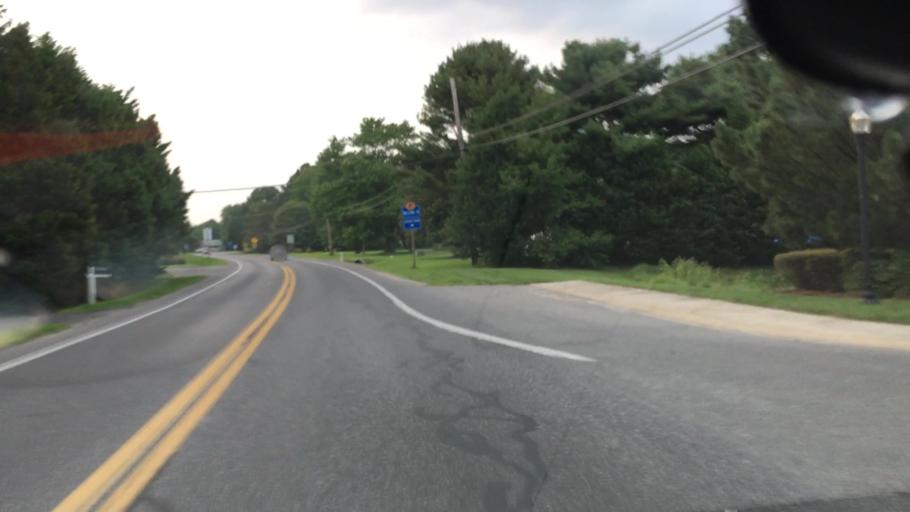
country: US
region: Delaware
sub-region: Sussex County
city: Ocean View
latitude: 38.5349
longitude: -75.0895
